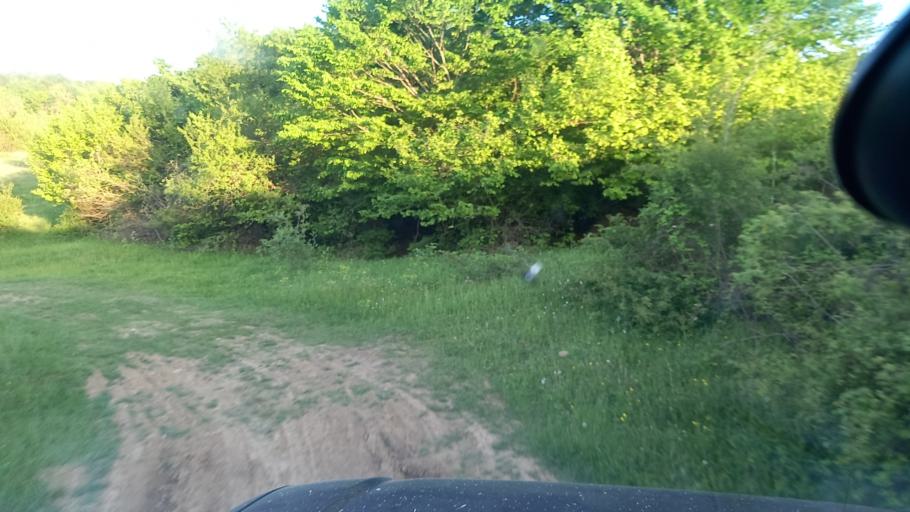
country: RU
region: Dagestan
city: Khuchni
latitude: 42.0070
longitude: 47.9718
